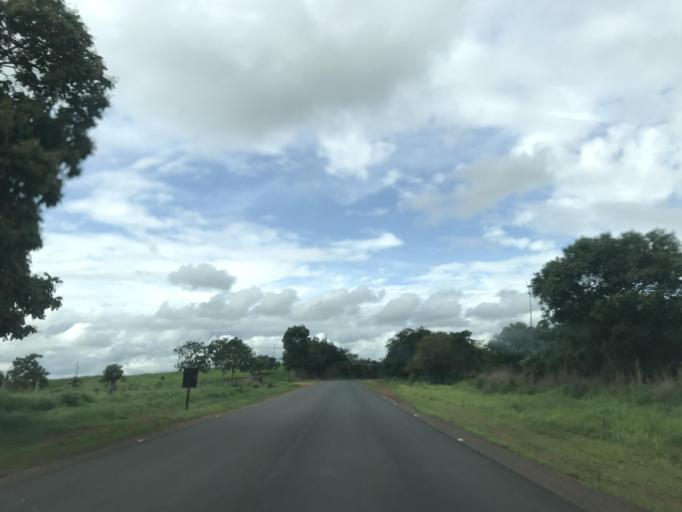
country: BR
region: Goias
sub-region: Bela Vista De Goias
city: Bela Vista de Goias
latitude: -17.0415
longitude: -48.6632
